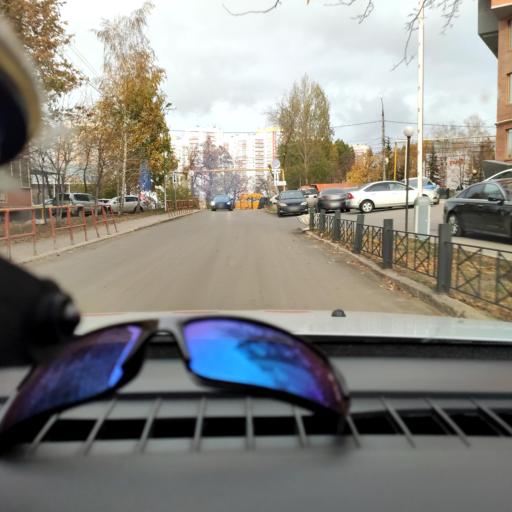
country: RU
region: Samara
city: Samara
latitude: 53.2377
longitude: 50.1804
